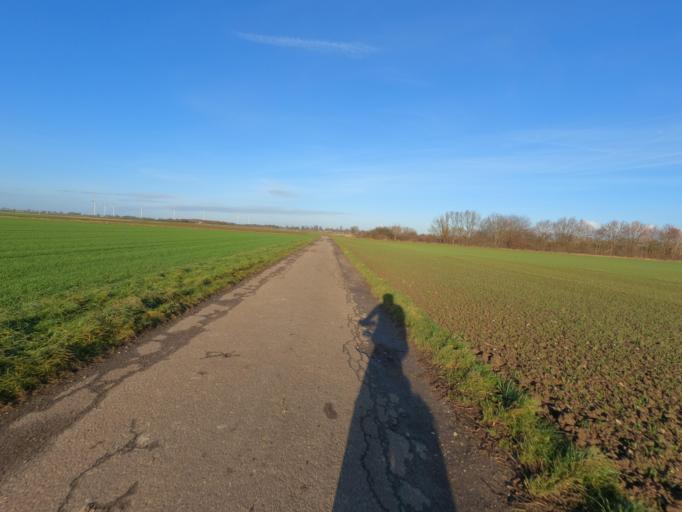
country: DE
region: North Rhine-Westphalia
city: Julich
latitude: 50.9444
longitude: 6.3925
